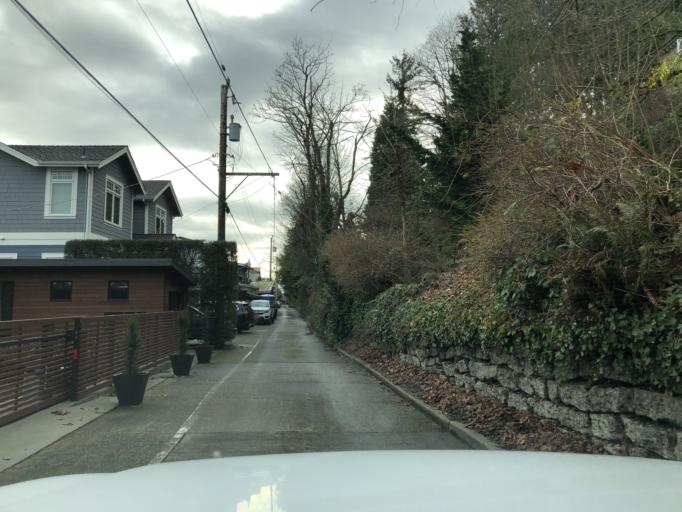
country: US
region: Washington
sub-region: King County
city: Inglewood-Finn Hill
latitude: 47.7101
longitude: -122.2764
